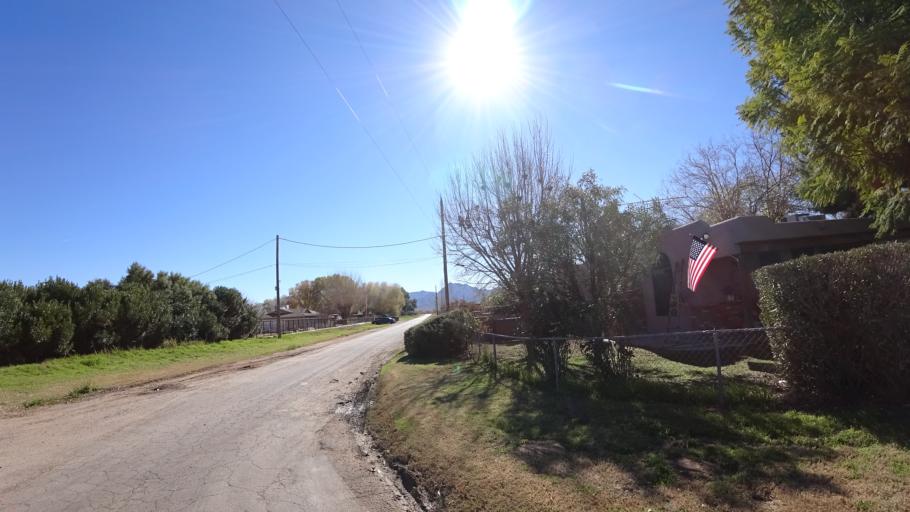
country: US
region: Arizona
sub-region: Maricopa County
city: Avondale
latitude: 33.3941
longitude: -112.3363
